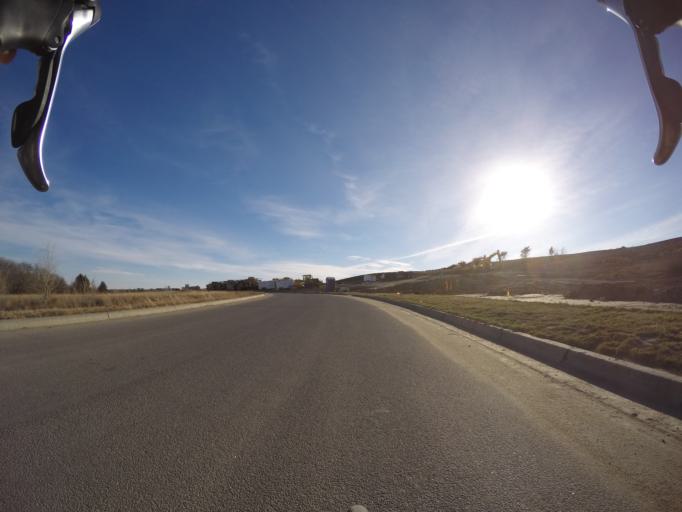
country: US
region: Kansas
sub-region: Riley County
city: Manhattan
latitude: 39.2112
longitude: -96.6356
